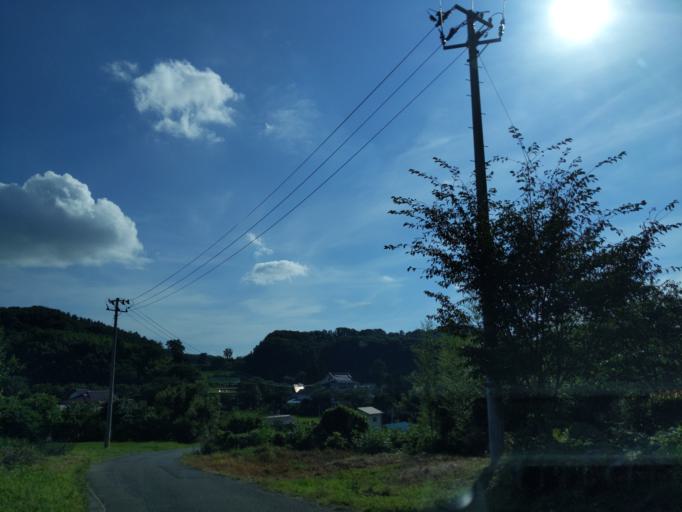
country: JP
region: Fukushima
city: Koriyama
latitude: 37.4010
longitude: 140.4280
